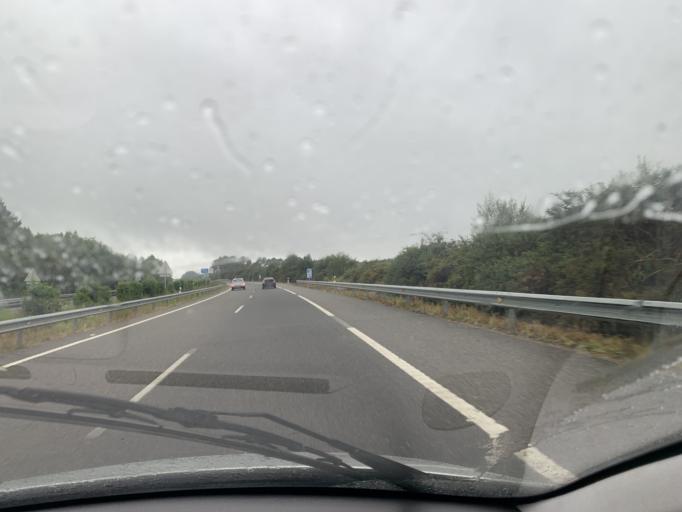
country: ES
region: Galicia
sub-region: Provincia de Lugo
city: Vilalba
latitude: 43.3274
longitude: -7.6122
